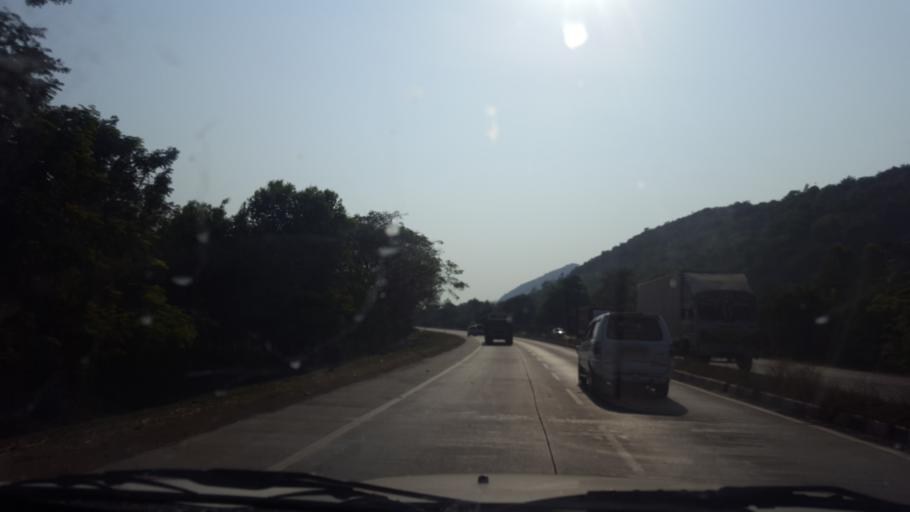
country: IN
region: Andhra Pradesh
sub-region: Vishakhapatnam
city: Elamanchili
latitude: 17.5559
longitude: 82.8462
